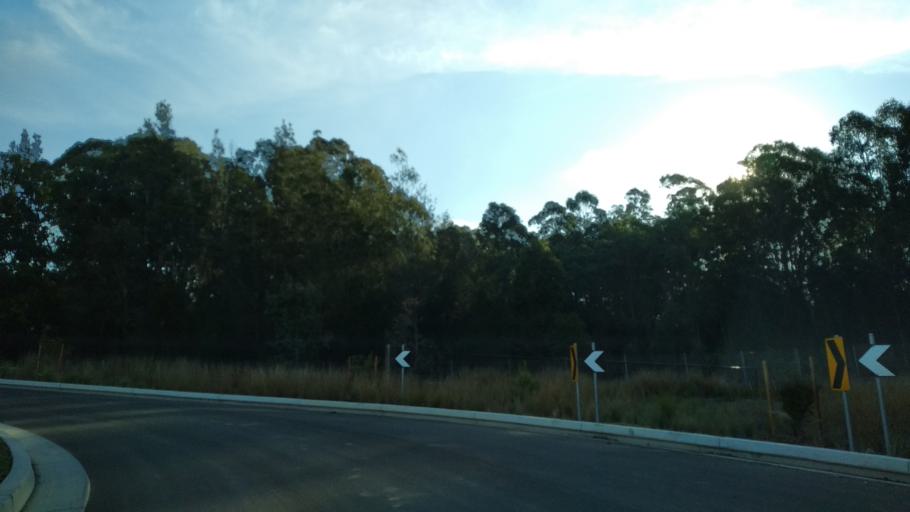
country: AU
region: New South Wales
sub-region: Penrith Municipality
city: Werrington County
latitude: -33.7328
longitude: 150.7498
